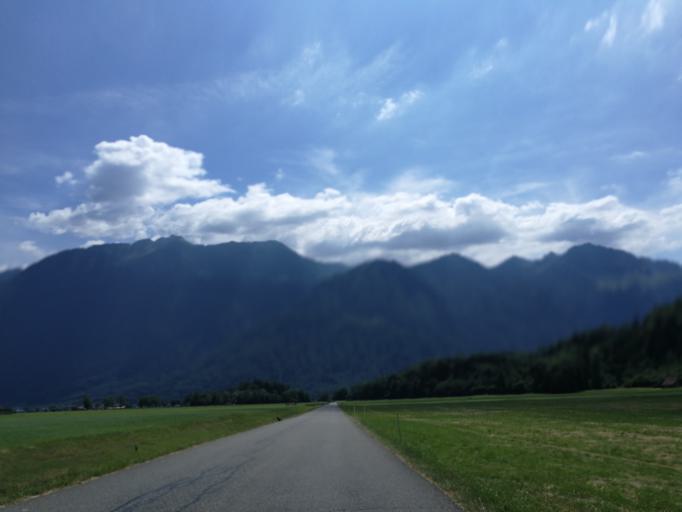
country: CH
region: Saint Gallen
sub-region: Wahlkreis See-Gaster
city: Benken
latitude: 47.1810
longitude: 9.0223
